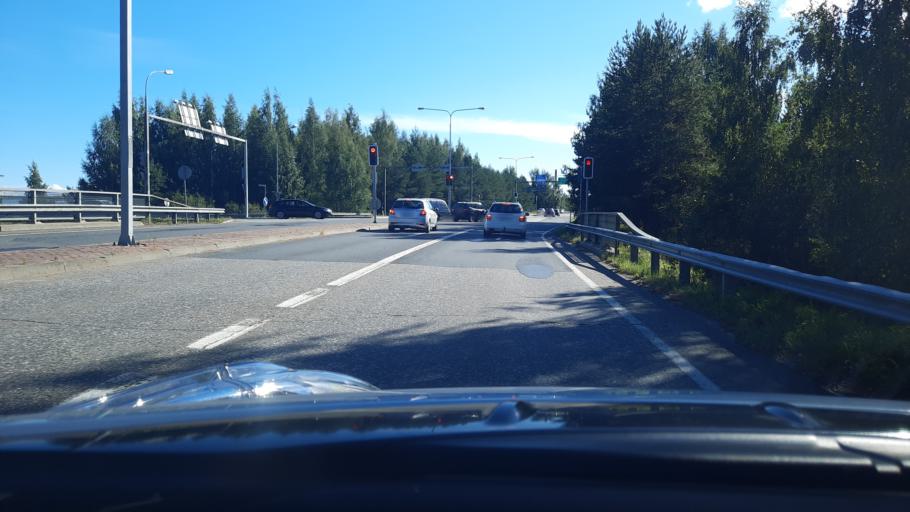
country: FI
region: North Karelia
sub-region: Joensuu
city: Joensuu
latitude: 62.6311
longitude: 29.7003
